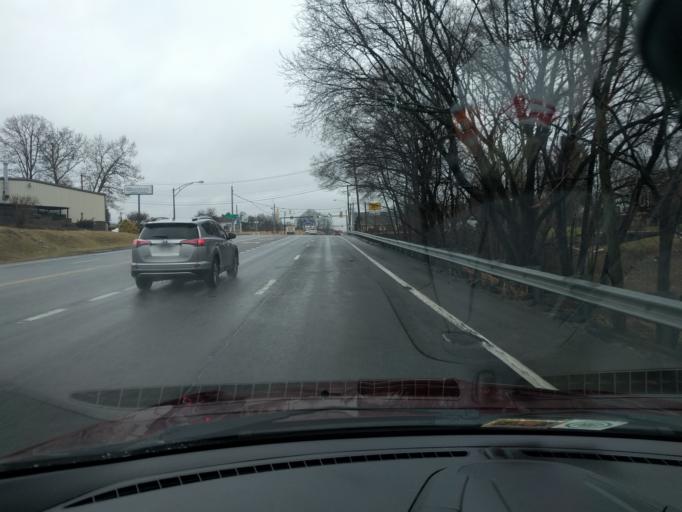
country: US
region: West Virginia
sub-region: Raleigh County
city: Beckley
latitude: 37.7701
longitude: -81.1956
